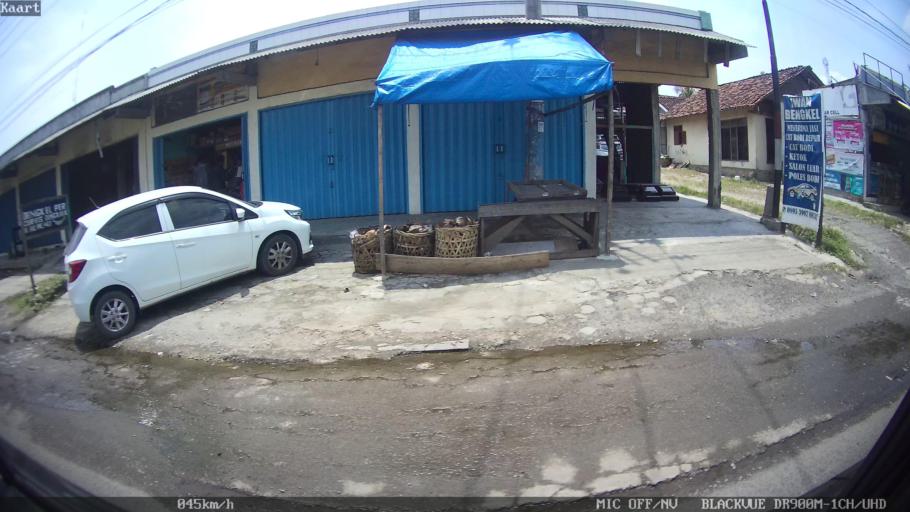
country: ID
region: Lampung
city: Natar
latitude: -5.2921
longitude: 105.1917
